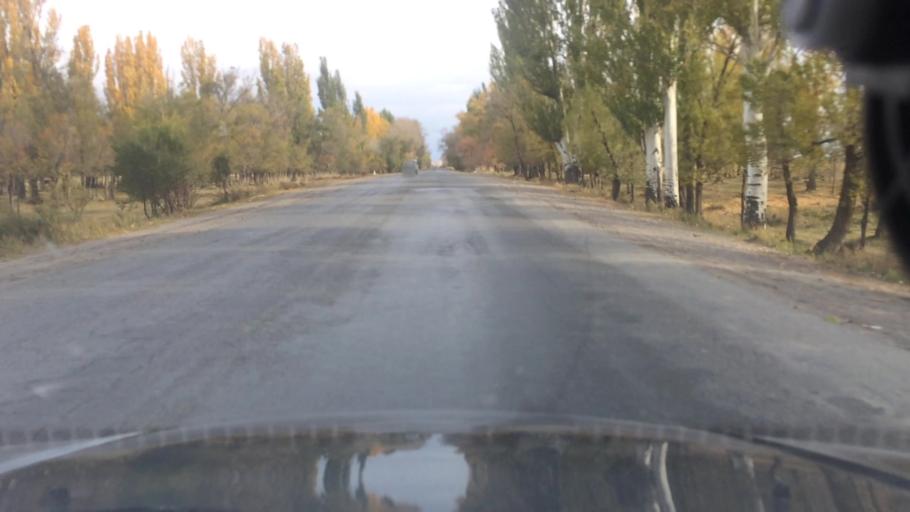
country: KG
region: Ysyk-Koel
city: Karakol
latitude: 42.5415
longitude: 78.3850
